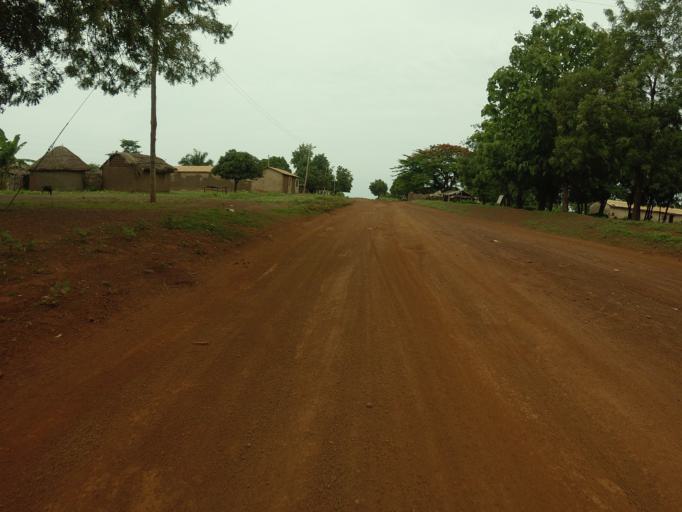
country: GH
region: Northern
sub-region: Yendi
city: Yendi
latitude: 9.0351
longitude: -0.0131
